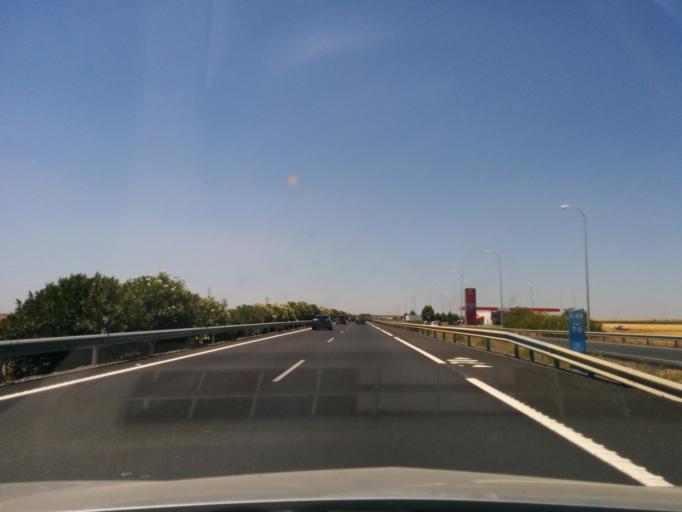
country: ES
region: Andalusia
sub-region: Provincia de Huelva
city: San Juan del Puerto
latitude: 37.3340
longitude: -6.7861
